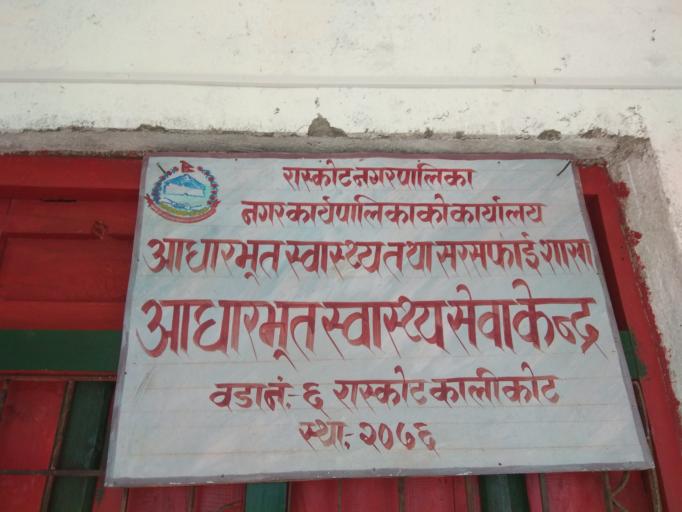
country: NP
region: Far Western
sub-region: Seti Zone
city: Achham
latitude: 29.2339
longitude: 81.6281
